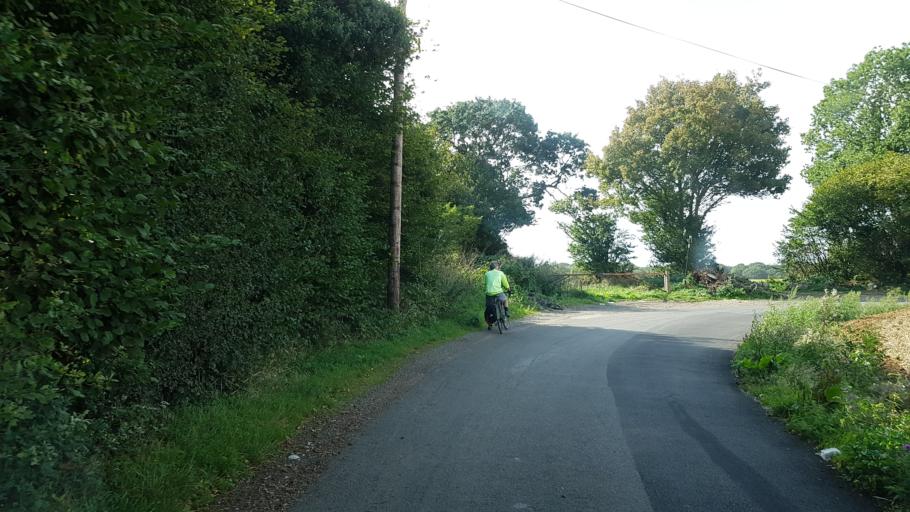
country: GB
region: England
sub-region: Kent
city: Harrietsham
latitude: 51.2381
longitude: 0.6138
